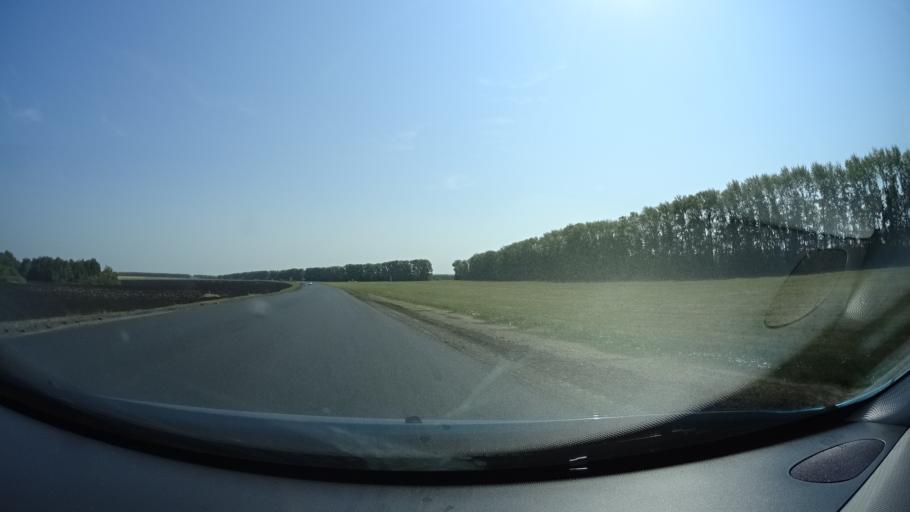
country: RU
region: Bashkortostan
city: Karmaskaly
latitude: 54.3875
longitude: 56.1357
